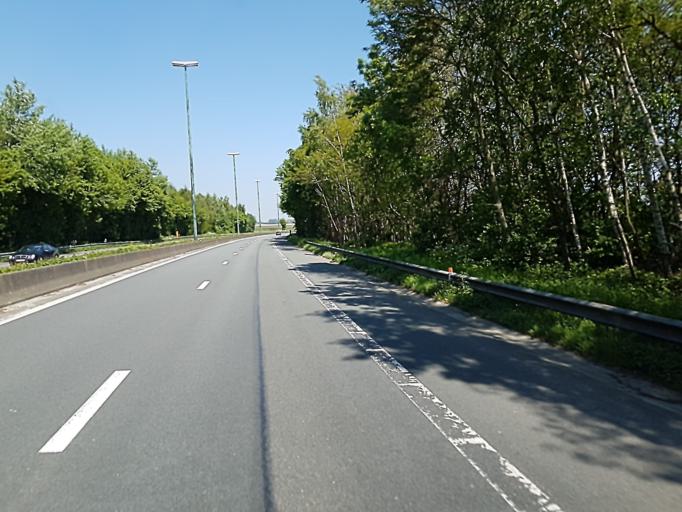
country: BE
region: Wallonia
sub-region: Province du Brabant Wallon
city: Genappe
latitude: 50.6066
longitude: 4.3907
